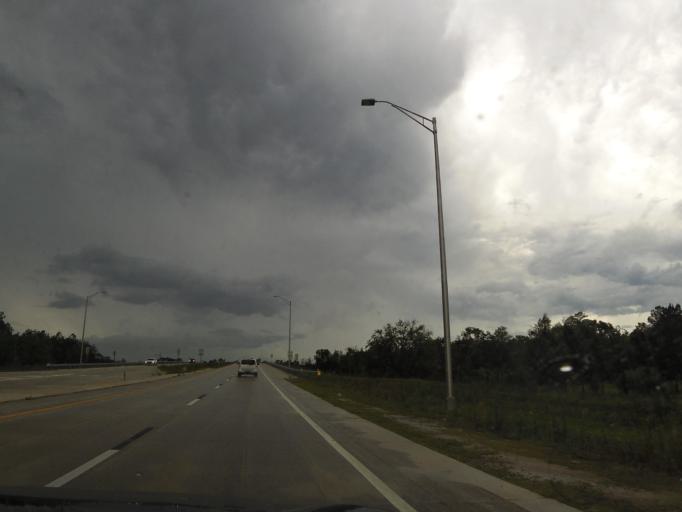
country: US
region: Florida
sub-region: Duval County
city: Baldwin
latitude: 30.3020
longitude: -81.9893
